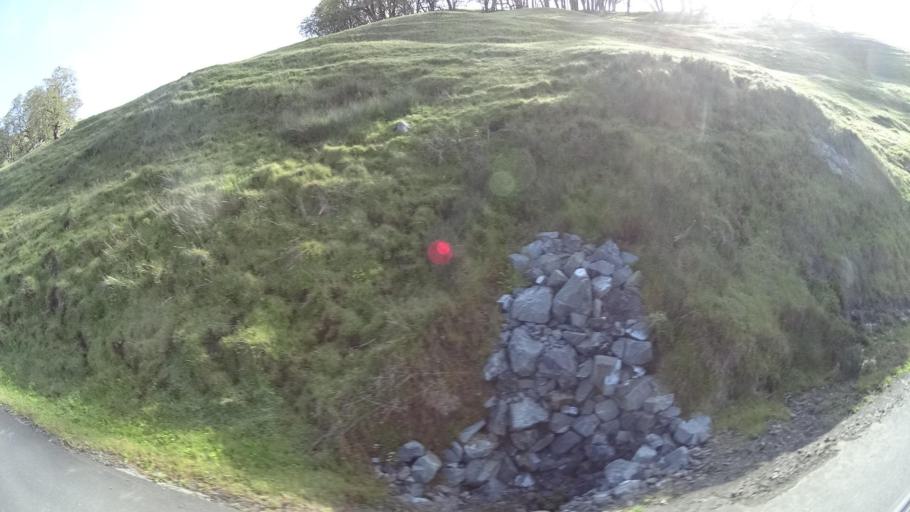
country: US
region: California
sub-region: Humboldt County
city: Blue Lake
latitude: 40.7144
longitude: -123.9371
